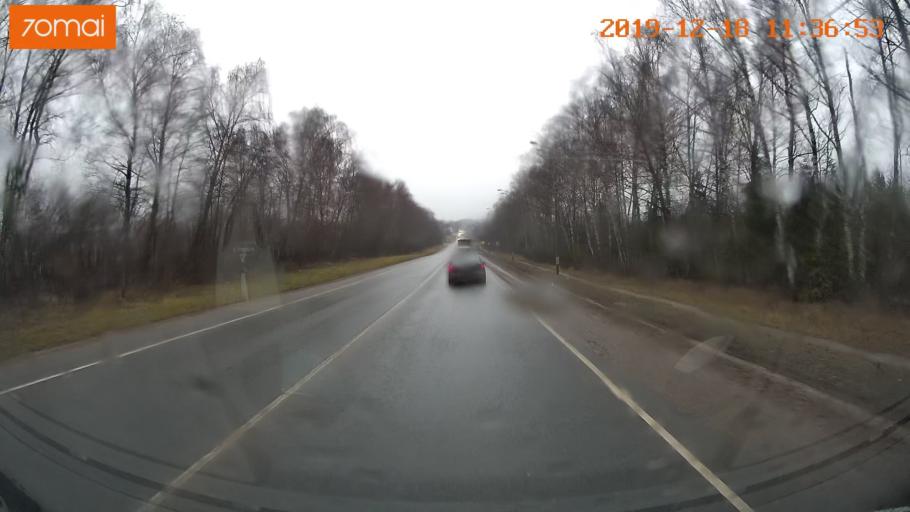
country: RU
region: Moskovskaya
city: Zvenigorod
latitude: 55.6859
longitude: 36.9002
